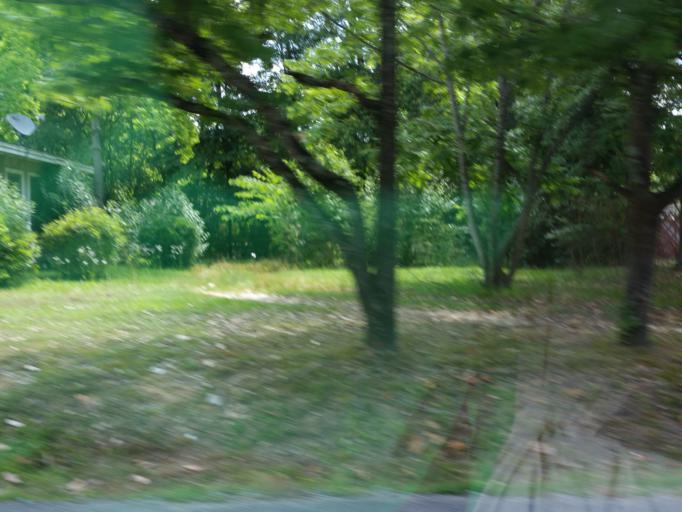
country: US
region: Mississippi
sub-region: Lauderdale County
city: Meridian
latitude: 32.3832
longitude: -88.7203
